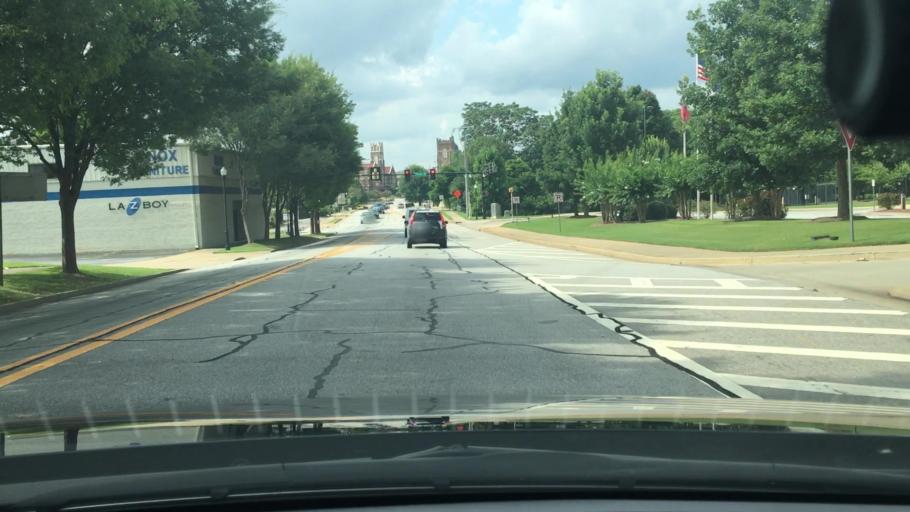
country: US
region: Georgia
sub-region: Coweta County
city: Newnan
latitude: 33.3691
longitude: -84.7990
